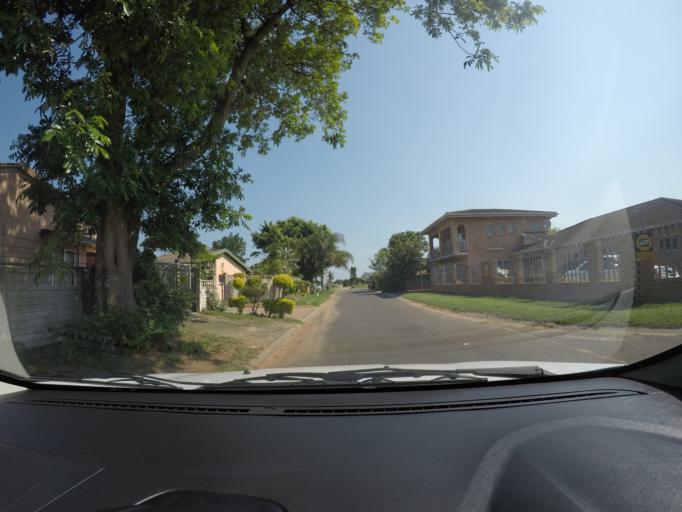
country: ZA
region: KwaZulu-Natal
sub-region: uThungulu District Municipality
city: Richards Bay
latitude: -28.7240
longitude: 32.0449
